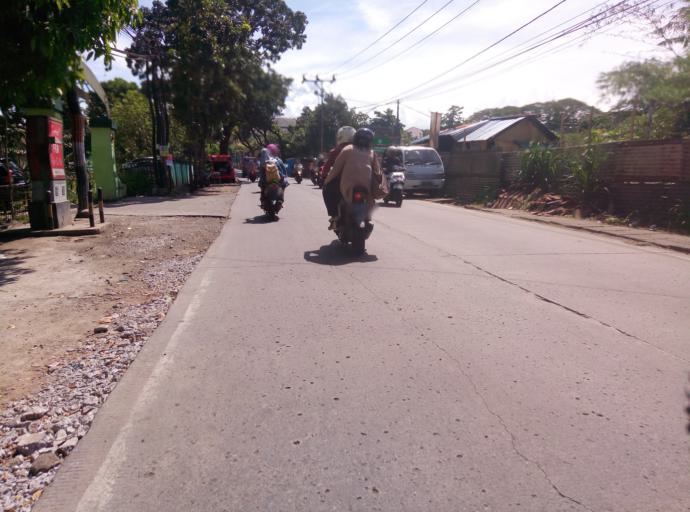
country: ID
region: West Java
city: Bandung
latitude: -6.8949
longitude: 107.6423
